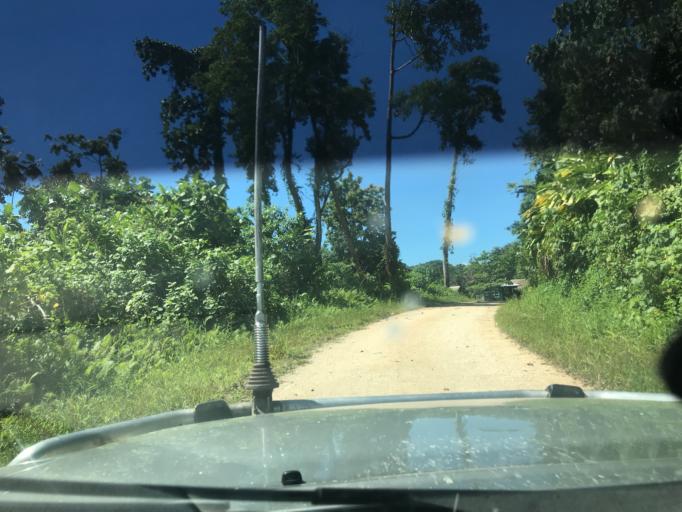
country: SB
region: Malaita
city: Auki
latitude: -8.7309
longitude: 160.9115
